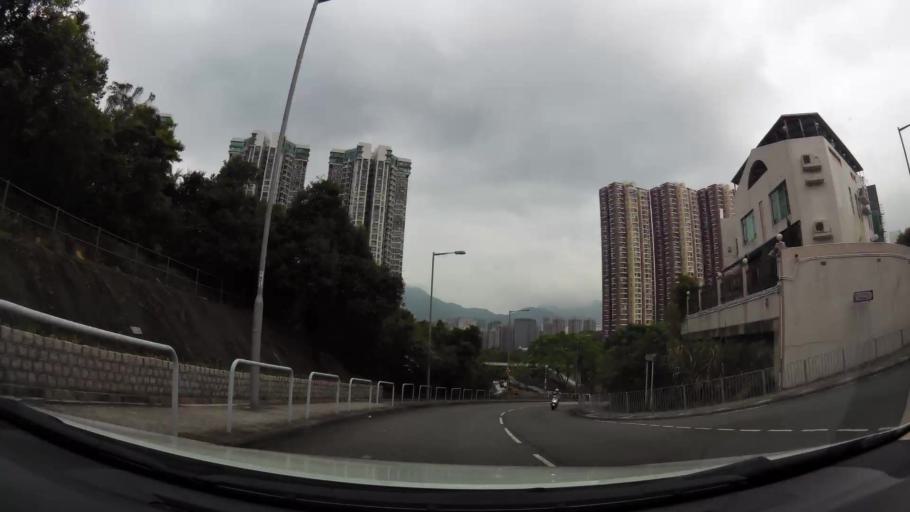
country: HK
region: Sha Tin
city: Sha Tin
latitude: 22.4005
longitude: 114.2002
